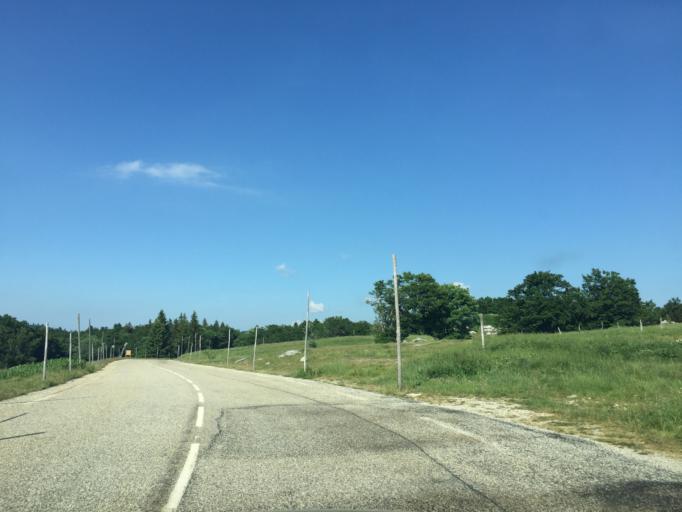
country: FR
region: Rhone-Alpes
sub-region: Departement de la Drome
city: Saint-Jean-en-Royans
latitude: 44.9013
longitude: 5.3320
